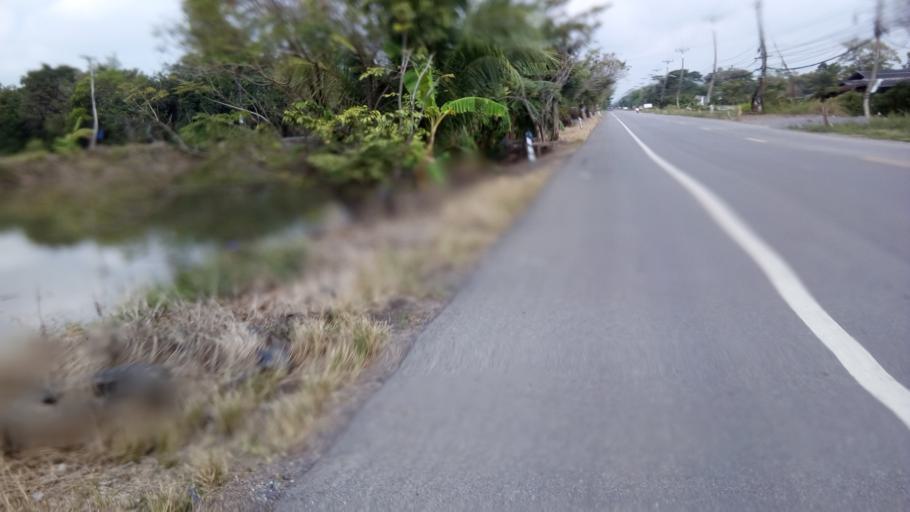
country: TH
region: Pathum Thani
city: Nong Suea
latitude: 14.1777
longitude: 100.8236
